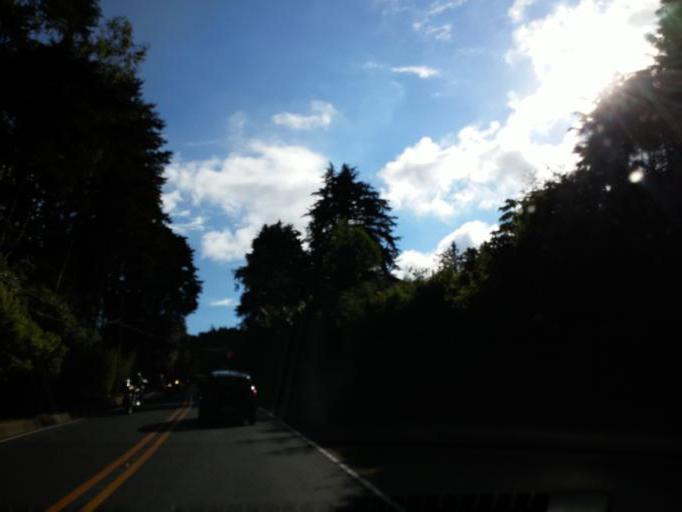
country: CR
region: San Jose
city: Salitrillos
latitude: 9.8335
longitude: -84.1039
